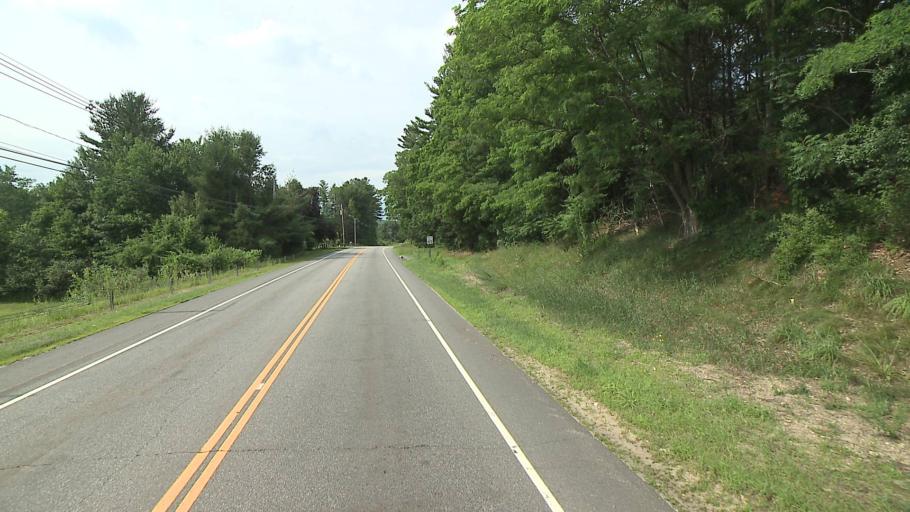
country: US
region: Connecticut
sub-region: Litchfield County
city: Winsted
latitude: 41.8799
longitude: -73.0765
